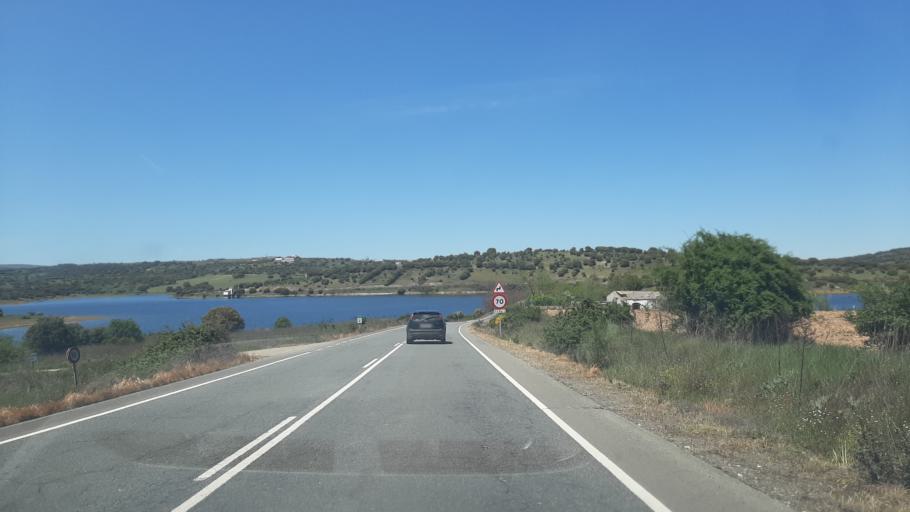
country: ES
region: Castille and Leon
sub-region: Provincia de Salamanca
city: Guijo de Avila
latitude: 40.5503
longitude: -5.6241
